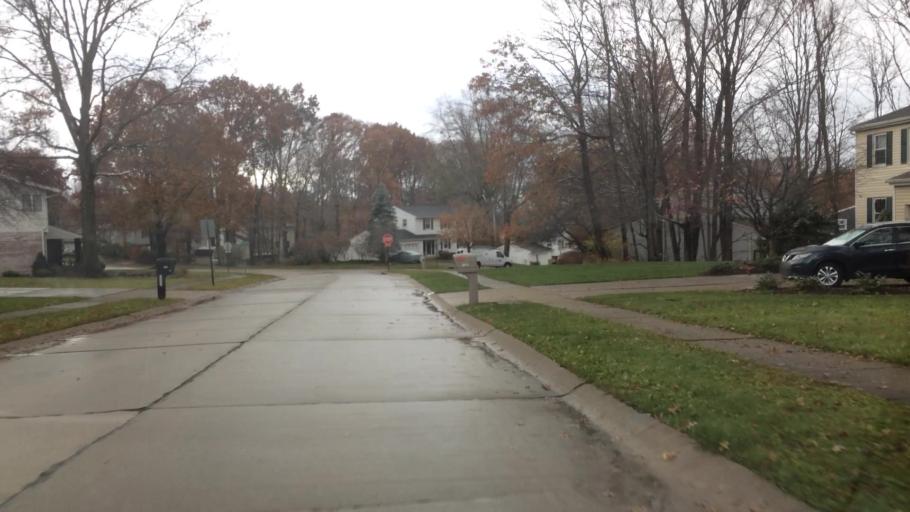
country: US
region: Ohio
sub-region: Summit County
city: Silver Lake
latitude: 41.1786
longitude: -81.4600
